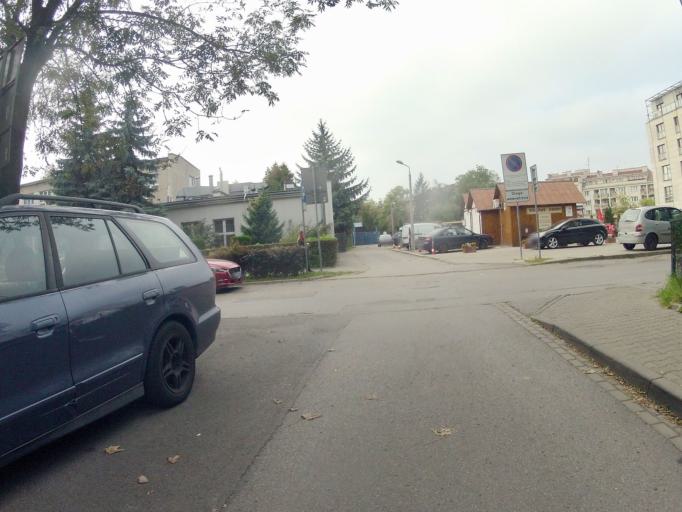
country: PL
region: Lesser Poland Voivodeship
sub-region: Krakow
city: Krakow
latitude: 50.0402
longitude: 19.9397
